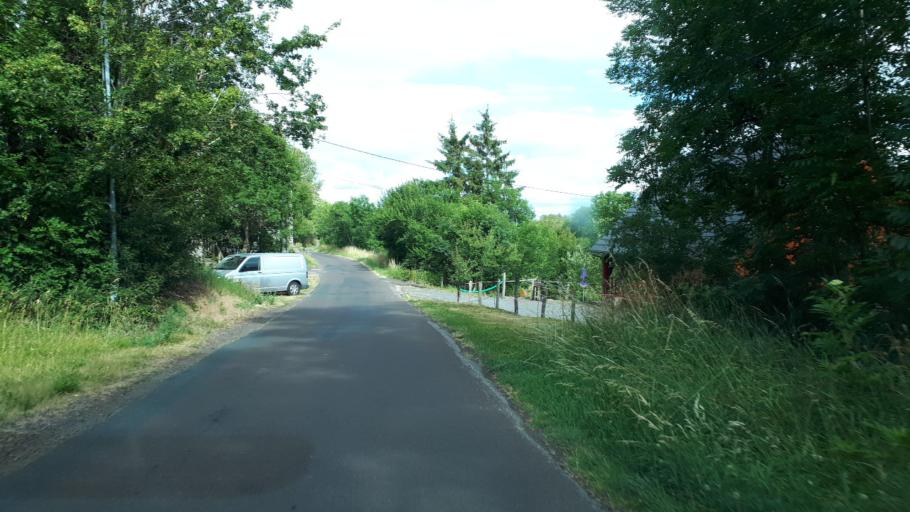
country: FR
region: Auvergne
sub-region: Departement du Puy-de-Dome
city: Aydat
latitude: 45.5930
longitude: 2.9632
